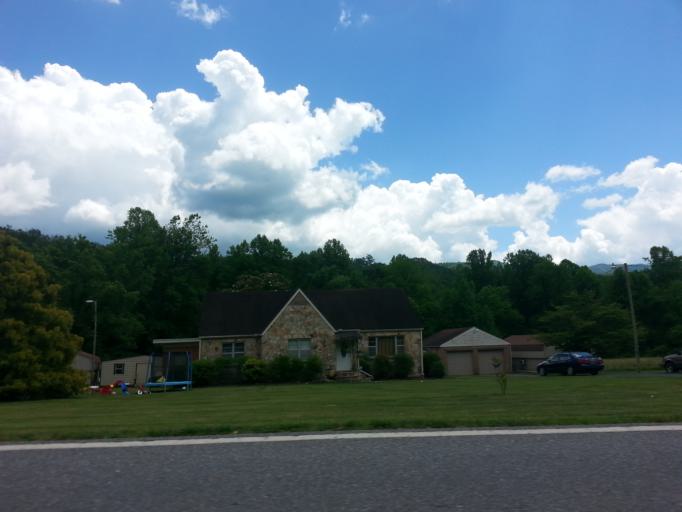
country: US
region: North Carolina
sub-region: Cherokee County
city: Andrews
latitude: 35.1948
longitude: -83.7844
